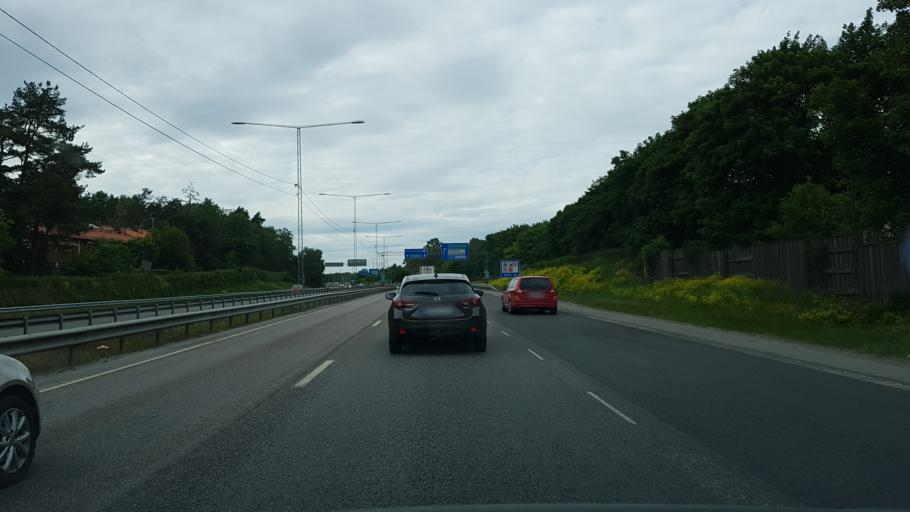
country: SE
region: Stockholm
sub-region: Stockholms Kommun
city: Arsta
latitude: 59.2542
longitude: 18.1002
